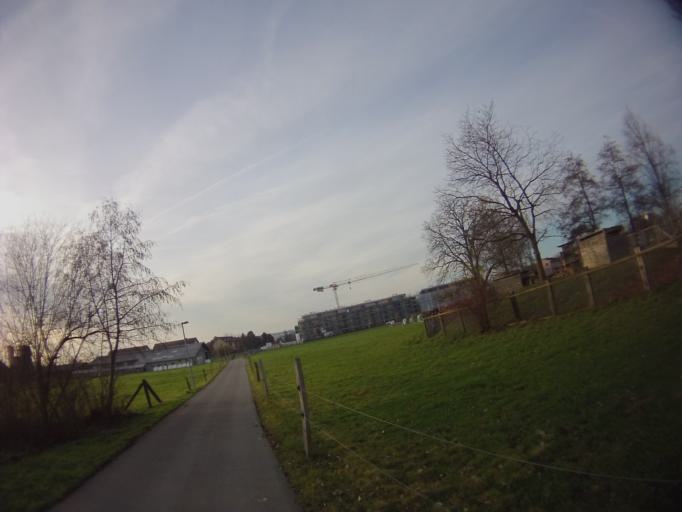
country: CH
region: Zug
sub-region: Zug
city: Steinhausen
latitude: 47.1808
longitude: 8.4952
